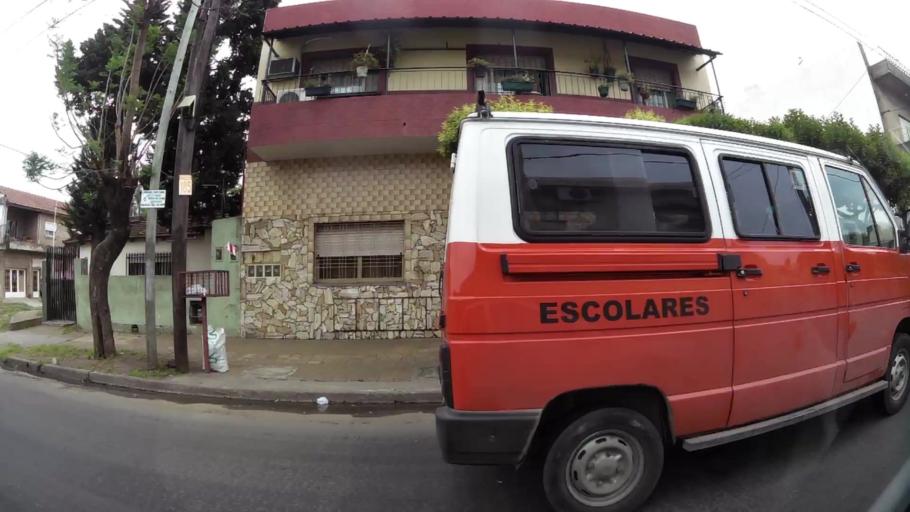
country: AR
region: Buenos Aires F.D.
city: Villa Lugano
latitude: -34.6742
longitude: -58.5155
